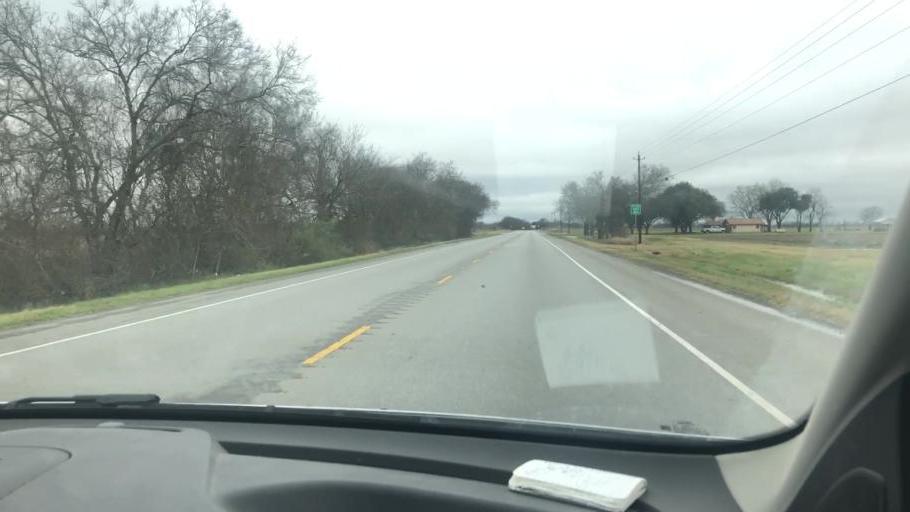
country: US
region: Texas
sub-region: Matagorda County
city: Bay City
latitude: 29.0704
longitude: -95.9715
